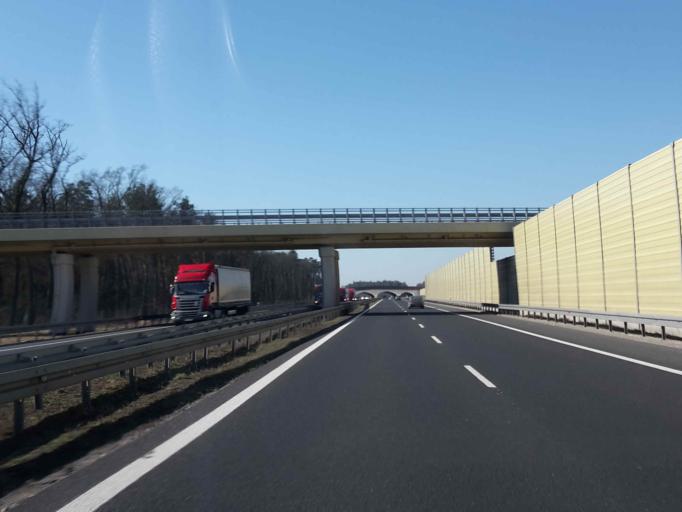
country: PL
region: Greater Poland Voivodeship
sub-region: Powiat poznanski
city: Pobiedziska
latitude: 52.4439
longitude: 17.3545
